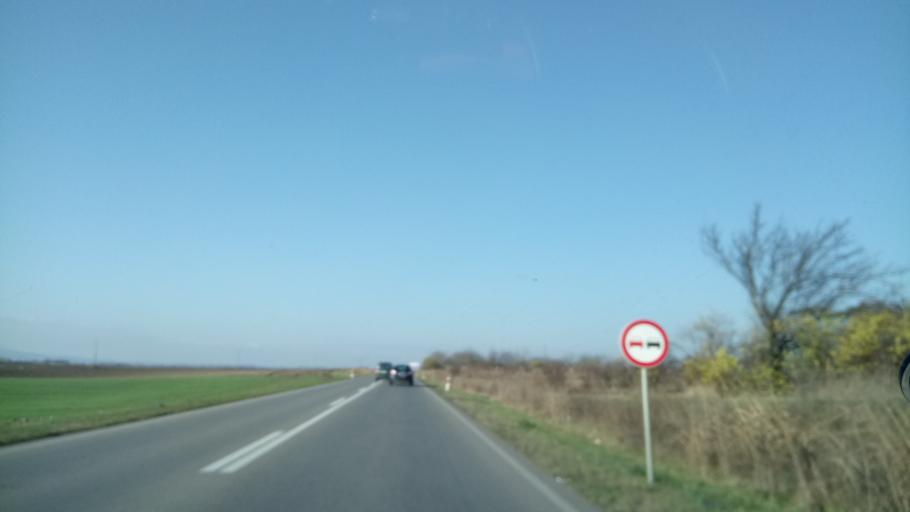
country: RS
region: Autonomna Pokrajina Vojvodina
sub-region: Sremski Okrug
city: Ingija
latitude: 45.0685
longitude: 20.0565
